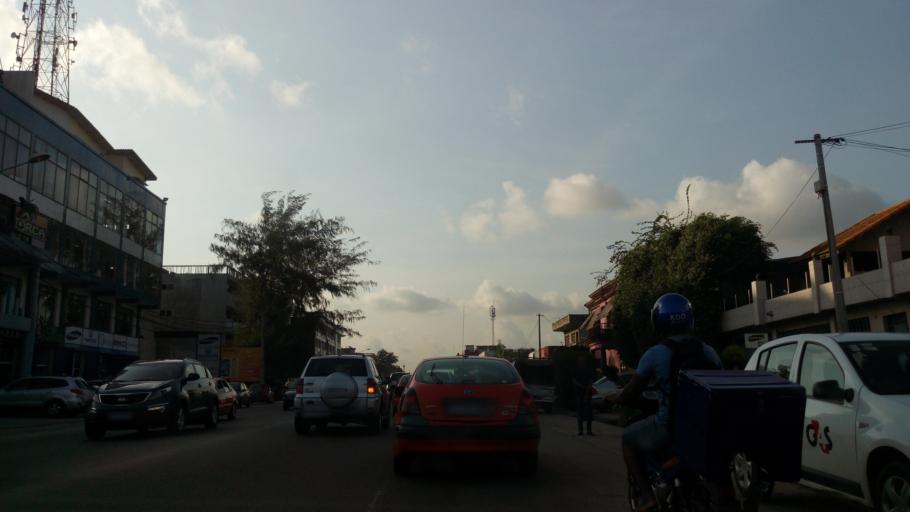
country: CI
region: Lagunes
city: Abobo
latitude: 5.4010
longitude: -3.9782
